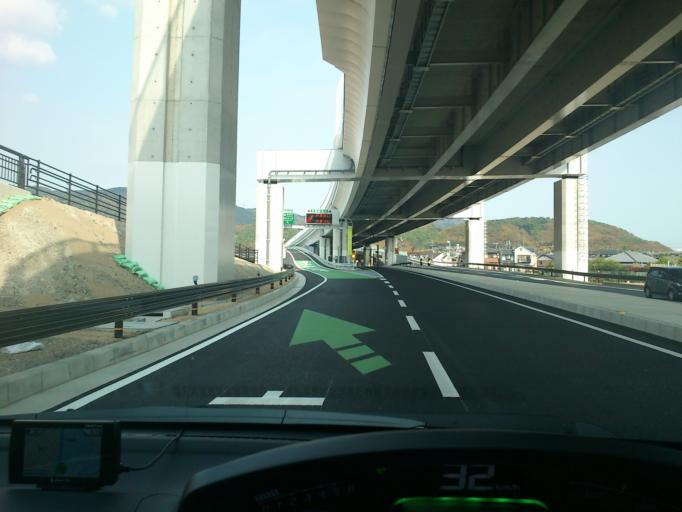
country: JP
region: Kyoto
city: Yawata
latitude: 34.9154
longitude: 135.6863
